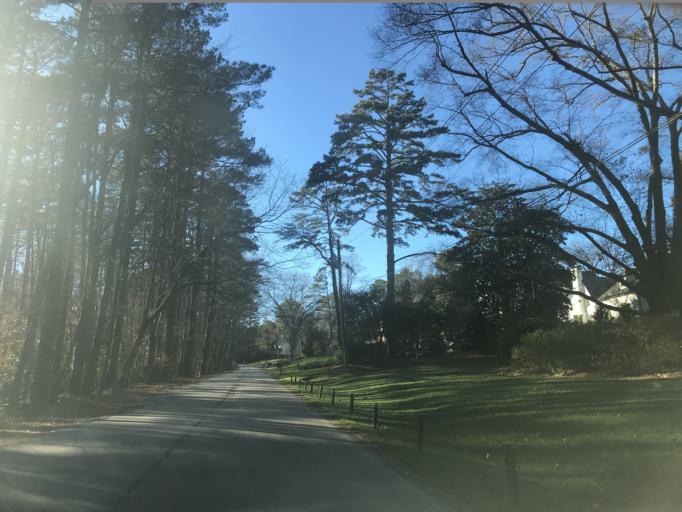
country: US
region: North Carolina
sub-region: Wake County
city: West Raleigh
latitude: 35.8272
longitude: -78.6621
